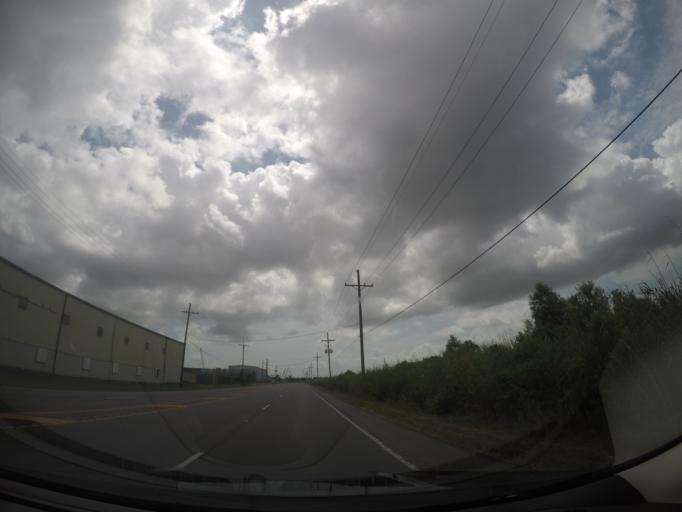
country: US
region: Louisiana
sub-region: Saint Tammany Parish
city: Eden Isle
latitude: 30.0767
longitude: -89.8517
